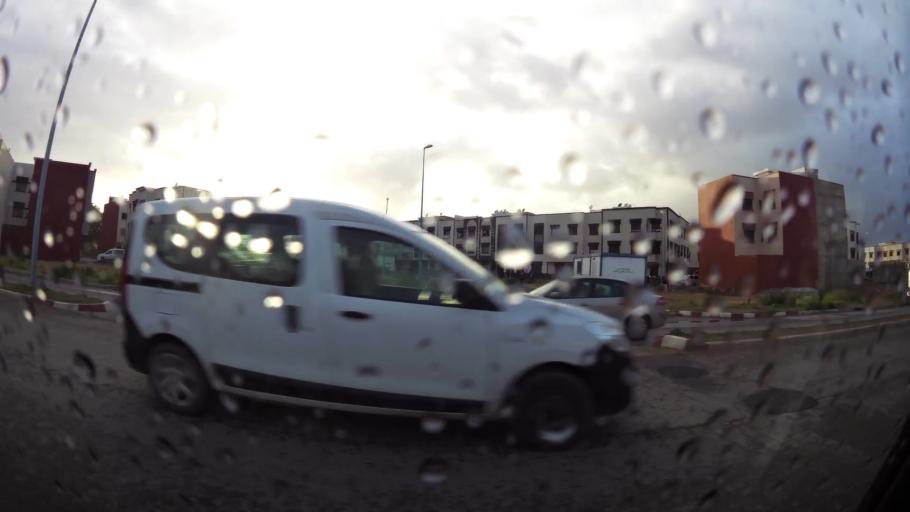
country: MA
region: Doukkala-Abda
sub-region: El-Jadida
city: El Jadida
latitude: 33.2329
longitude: -8.4857
